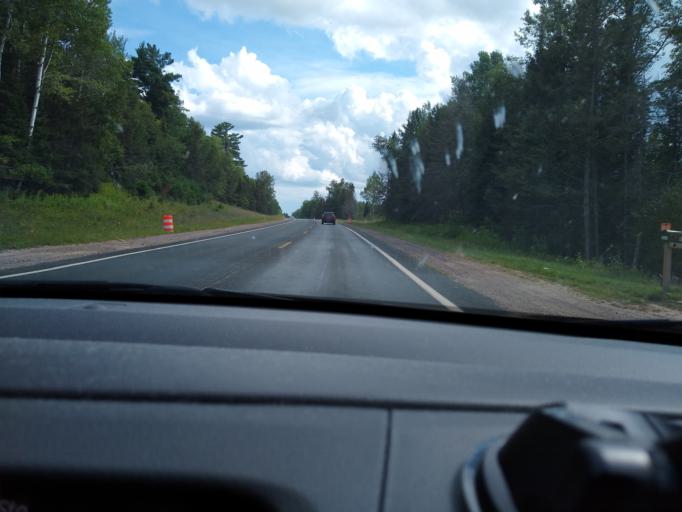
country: US
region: Michigan
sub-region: Iron County
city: Crystal Falls
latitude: 46.2694
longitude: -88.0177
